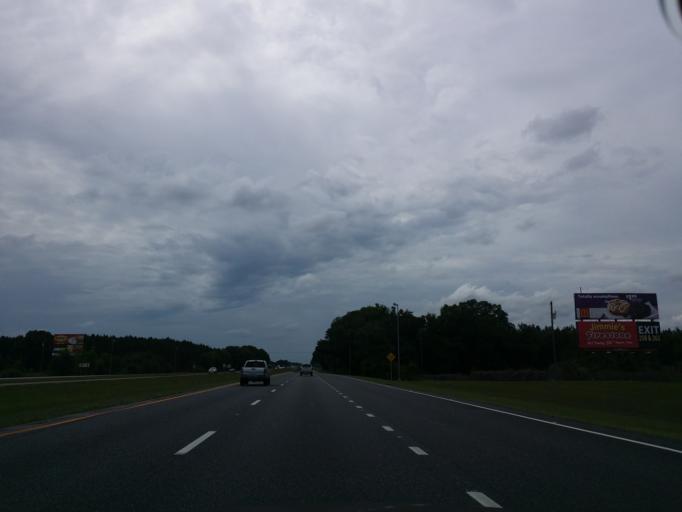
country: US
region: Florida
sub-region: Madison County
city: Madison
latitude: 30.3760
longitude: -83.2801
